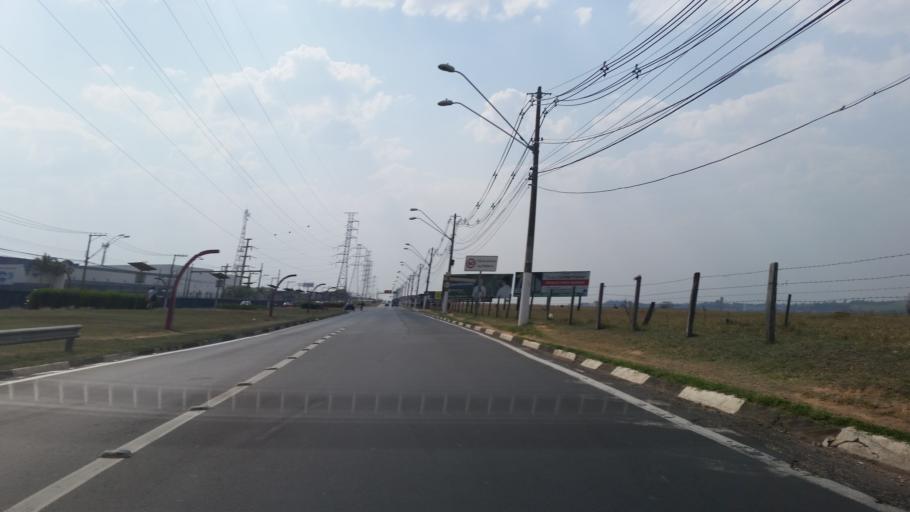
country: BR
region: Sao Paulo
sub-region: Hortolandia
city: Hortolandia
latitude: -22.8950
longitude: -47.1889
